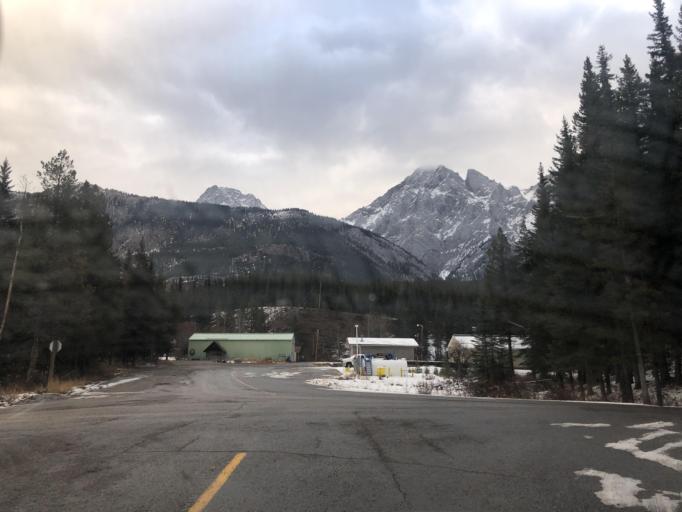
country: CA
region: Alberta
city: Canmore
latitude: 50.7130
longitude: -115.1180
